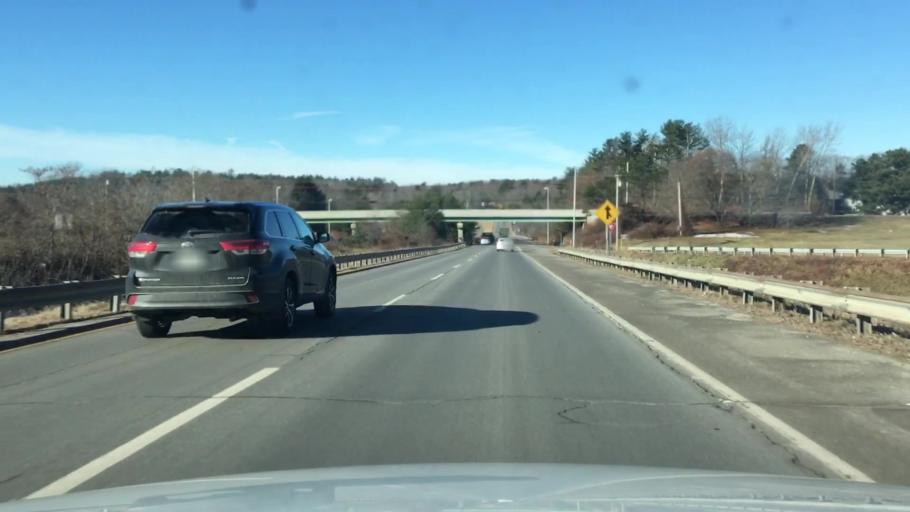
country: US
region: Maine
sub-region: Sagadahoc County
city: Bath
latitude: 43.9172
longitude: -69.8601
